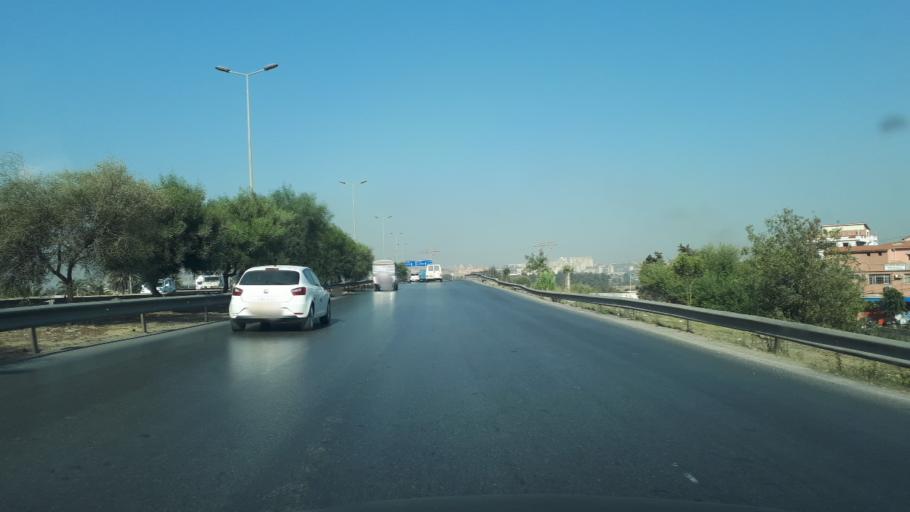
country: DZ
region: Tipaza
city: Baraki
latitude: 36.6826
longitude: 3.1015
